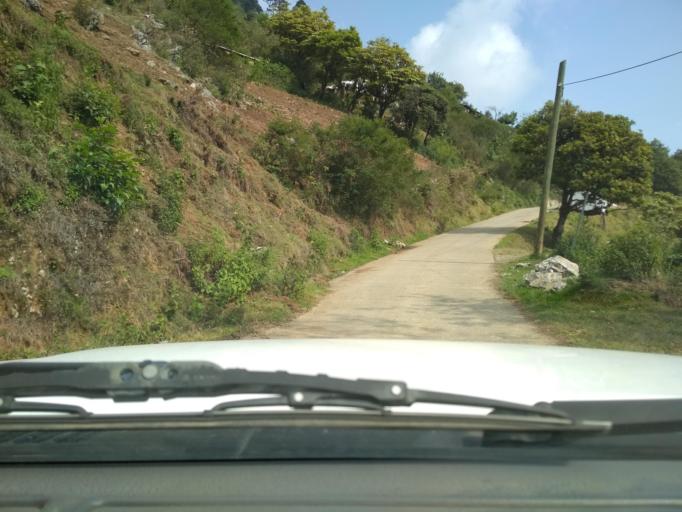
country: MX
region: Veracruz
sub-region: Camerino Z. Mendoza
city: Necoxtla
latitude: 18.7668
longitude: -97.1539
